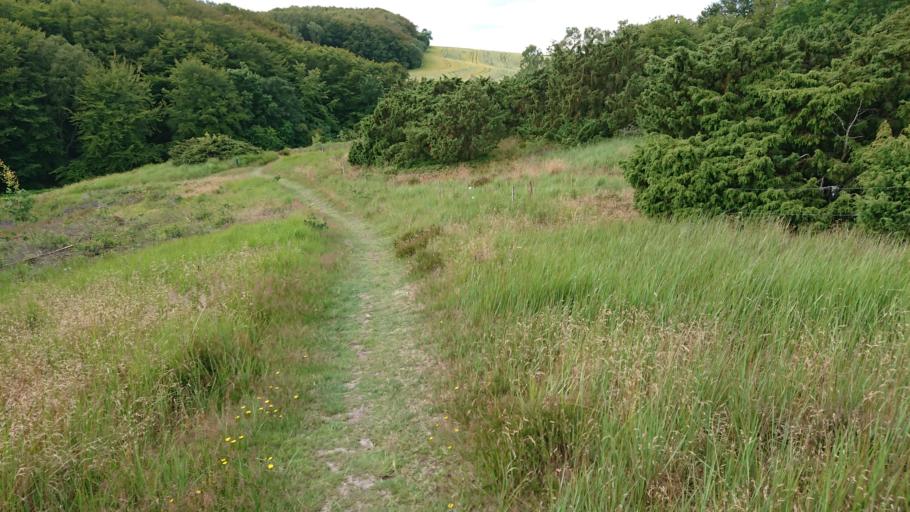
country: DK
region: North Denmark
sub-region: Hjorring Kommune
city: Sindal
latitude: 57.4521
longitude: 10.3339
